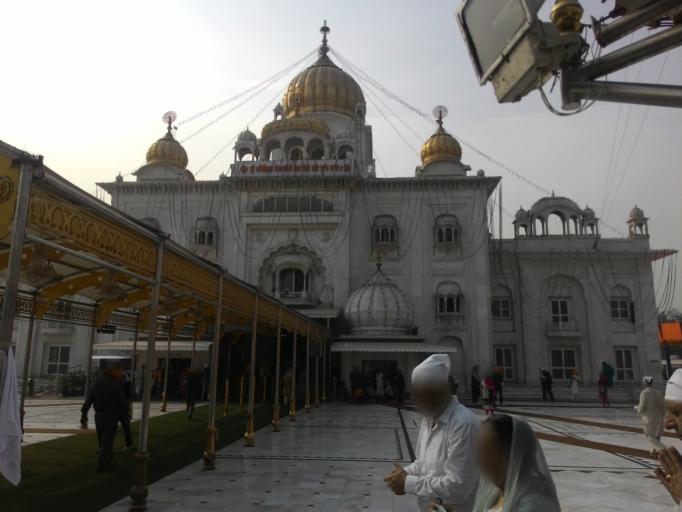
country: IN
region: NCT
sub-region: New Delhi
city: New Delhi
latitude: 28.6267
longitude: 77.2093
